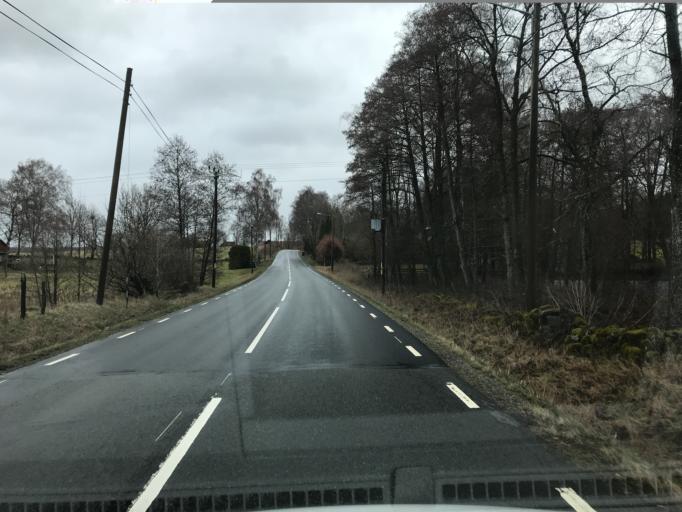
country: SE
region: Skane
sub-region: Perstorps Kommun
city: Perstorp
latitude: 56.0290
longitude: 13.4277
